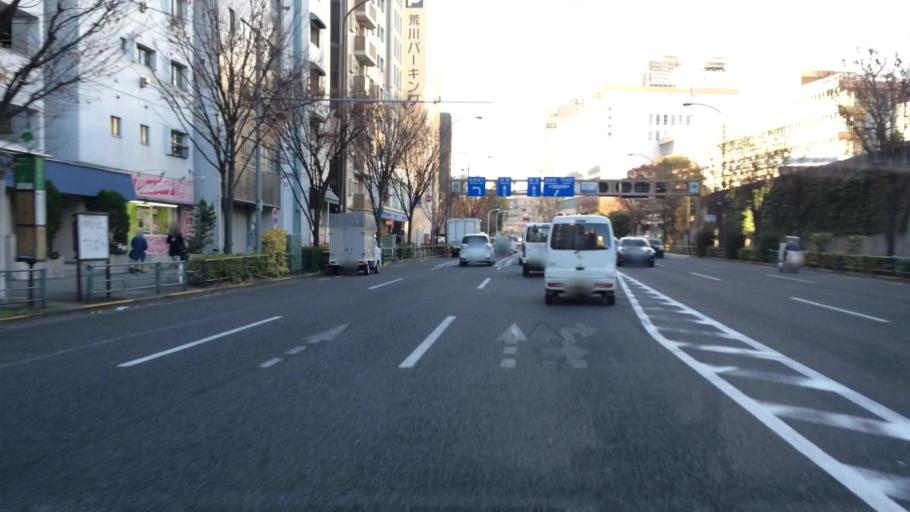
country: JP
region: Tokyo
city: Tokyo
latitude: 35.6916
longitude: 139.7271
